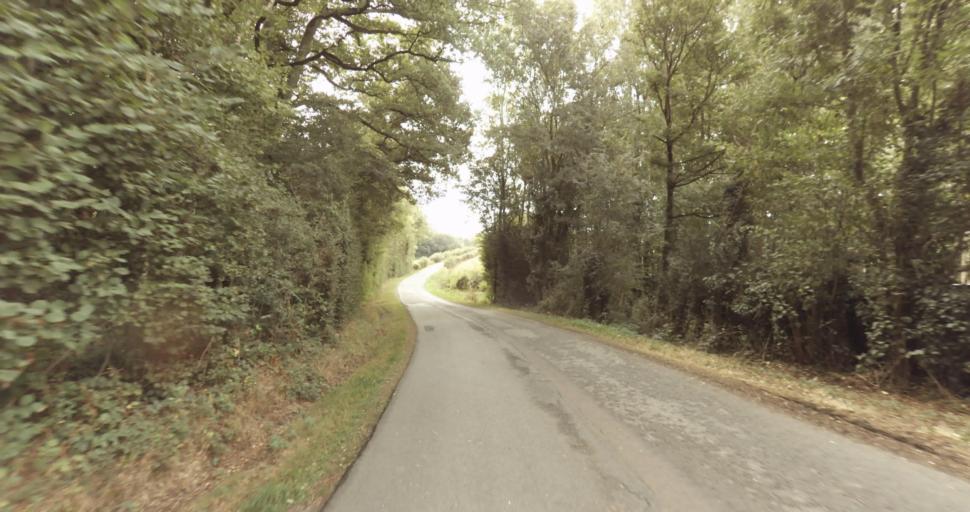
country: FR
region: Lower Normandy
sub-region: Departement du Calvados
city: La Vespiere
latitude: 48.9526
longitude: 0.3604
